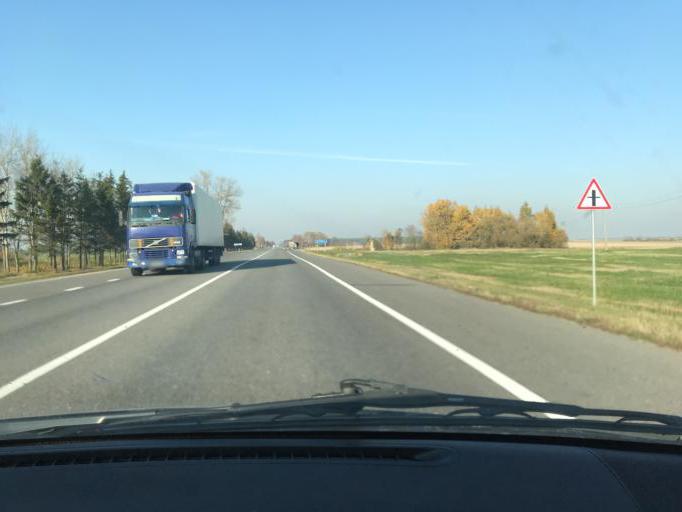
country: BY
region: Mogilev
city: Shklow
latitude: 54.2683
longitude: 30.4499
